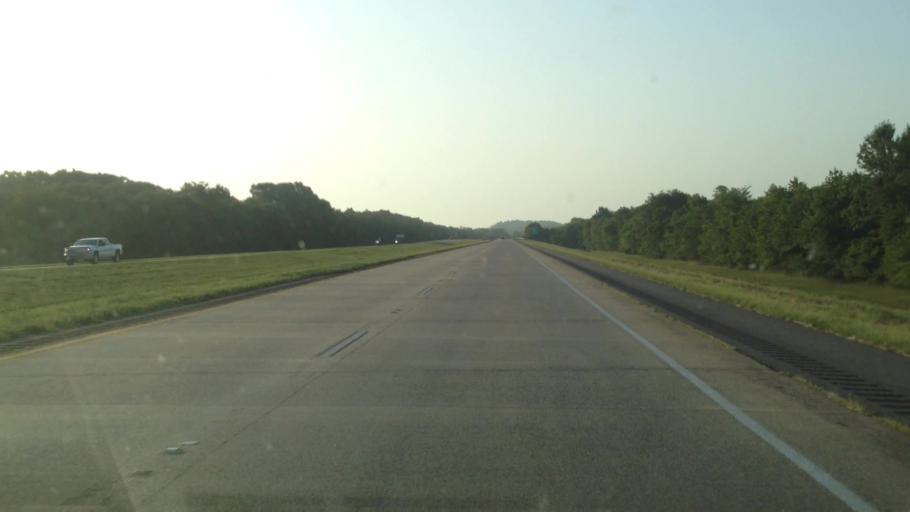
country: US
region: Louisiana
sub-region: Grant Parish
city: Colfax
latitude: 31.5043
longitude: -92.8801
